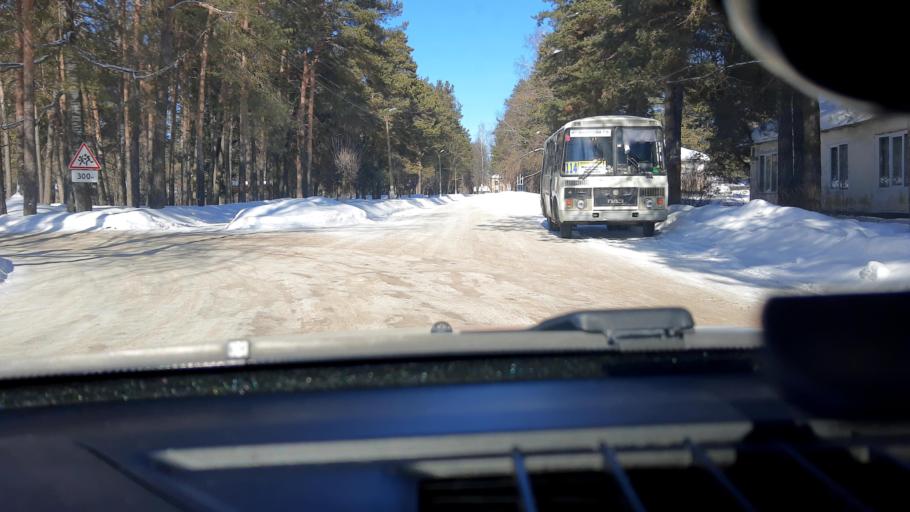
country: RU
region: Nizjnij Novgorod
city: Yuganets
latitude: 56.2459
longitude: 43.2319
